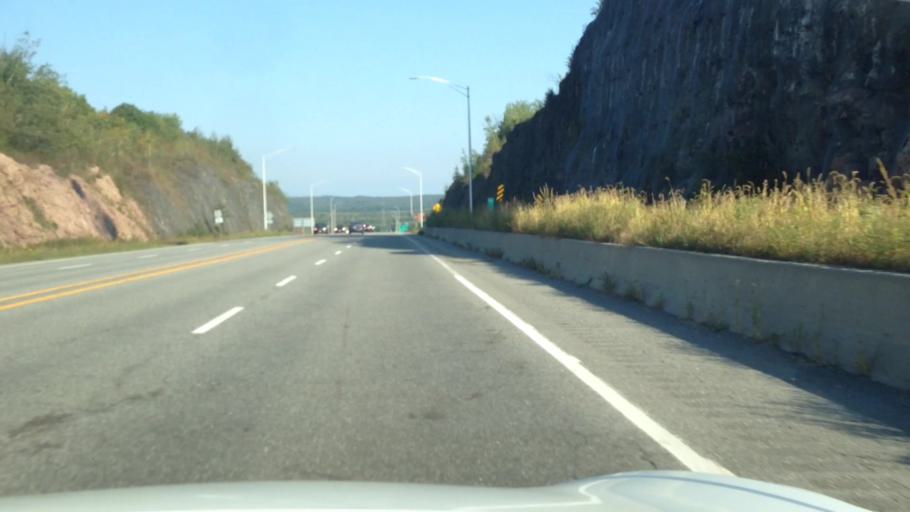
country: CA
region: Ontario
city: Clarence-Rockland
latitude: 45.5978
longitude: -75.3865
